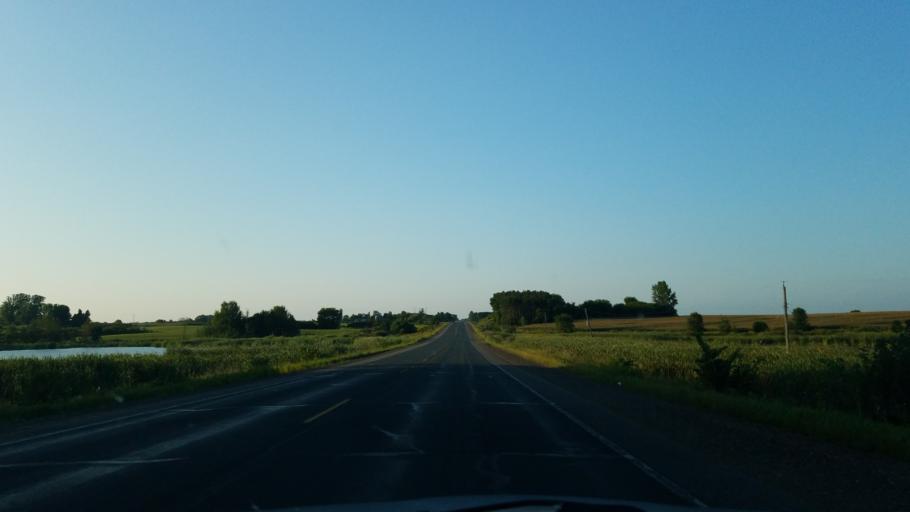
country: US
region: Wisconsin
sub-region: Polk County
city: Clear Lake
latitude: 45.2189
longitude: -92.2843
